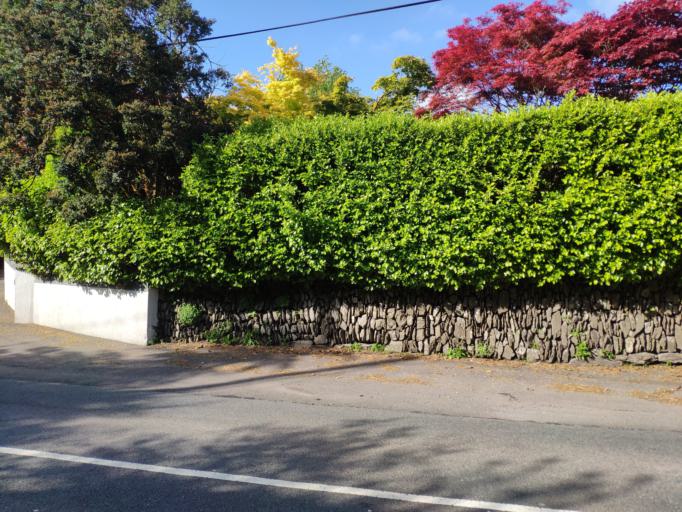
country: IE
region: Munster
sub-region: County Cork
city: Blarney
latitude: 51.9048
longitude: -8.5374
